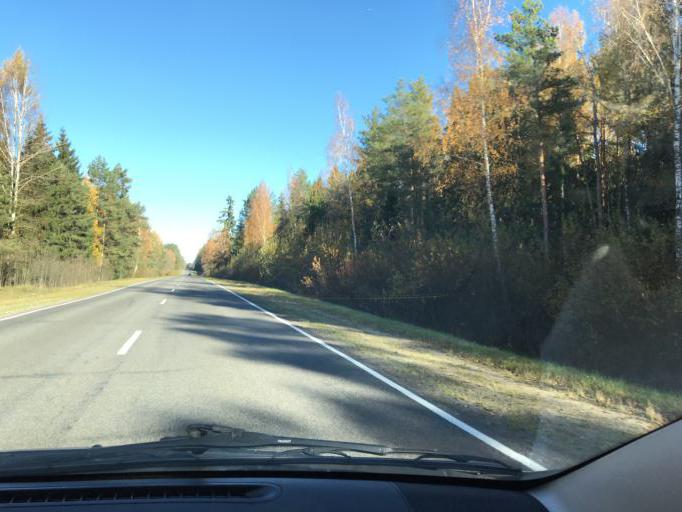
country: BY
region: Vitebsk
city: Lyepyel'
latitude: 54.9503
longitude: 28.7419
